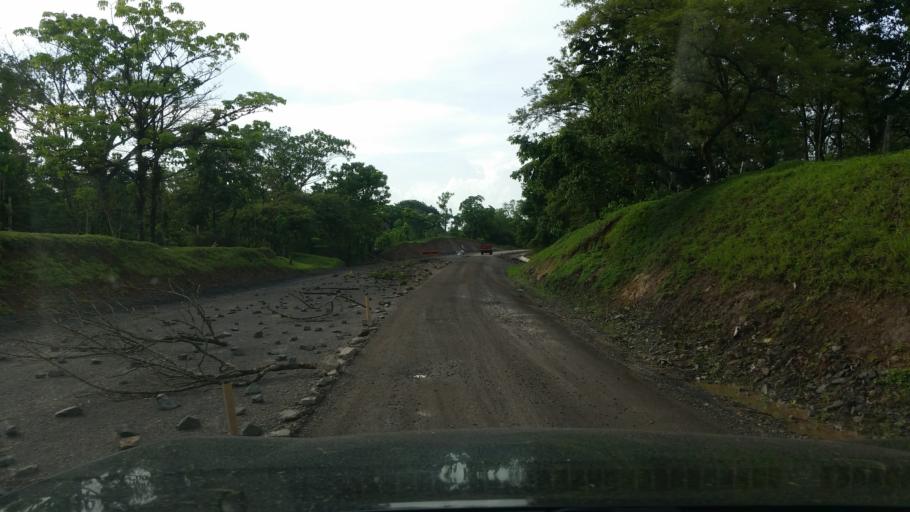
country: NI
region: Matagalpa
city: Rio Blanco
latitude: 13.0840
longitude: -85.0616
